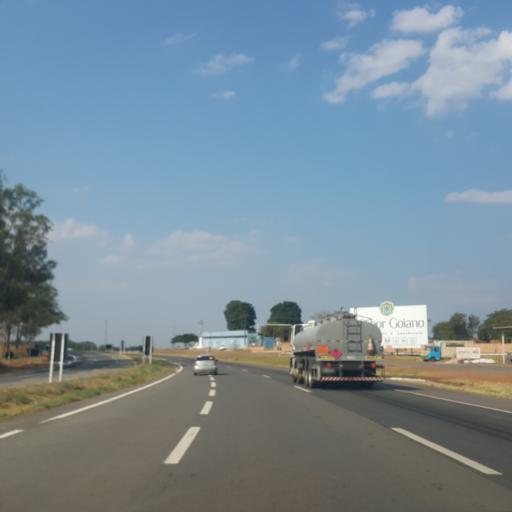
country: BR
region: Goias
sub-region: Abadiania
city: Abadiania
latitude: -16.1916
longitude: -48.7051
